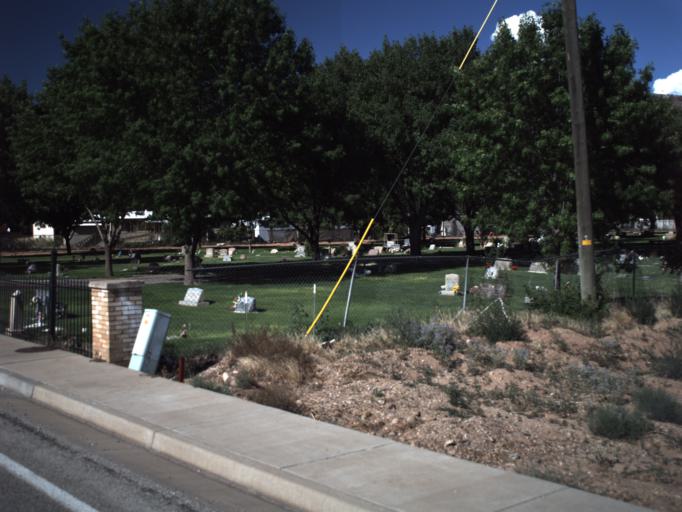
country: US
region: Utah
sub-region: Washington County
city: LaVerkin
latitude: 37.2121
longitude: -113.2721
